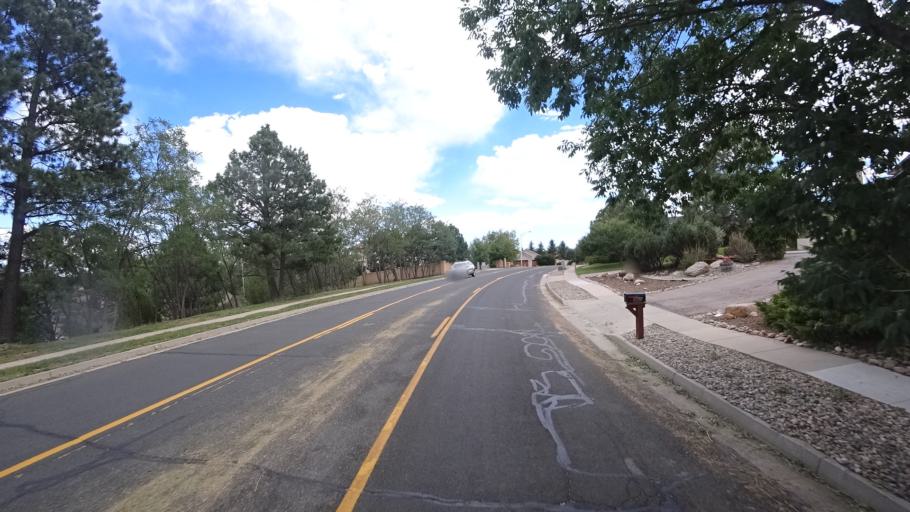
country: US
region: Colorado
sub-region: El Paso County
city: Stratmoor
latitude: 38.7754
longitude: -104.8272
